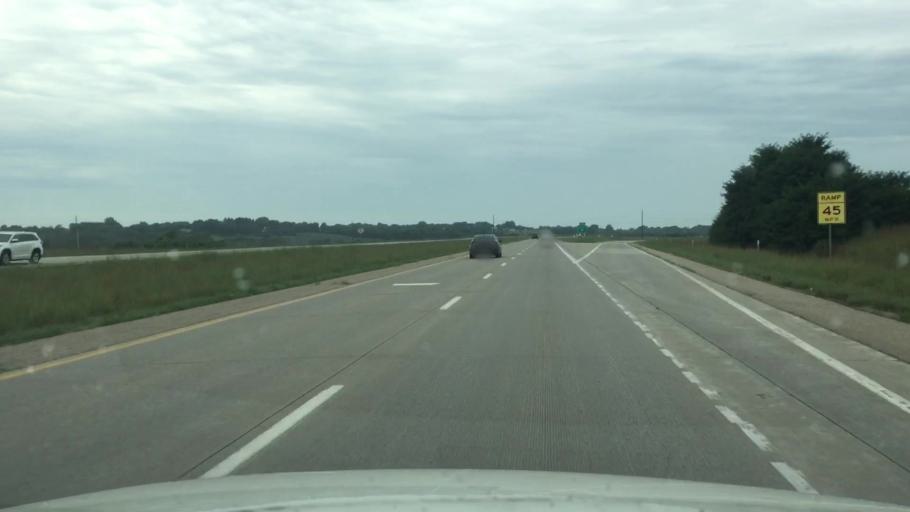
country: US
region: Iowa
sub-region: Warren County
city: Norwalk
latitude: 41.4984
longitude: -93.6173
